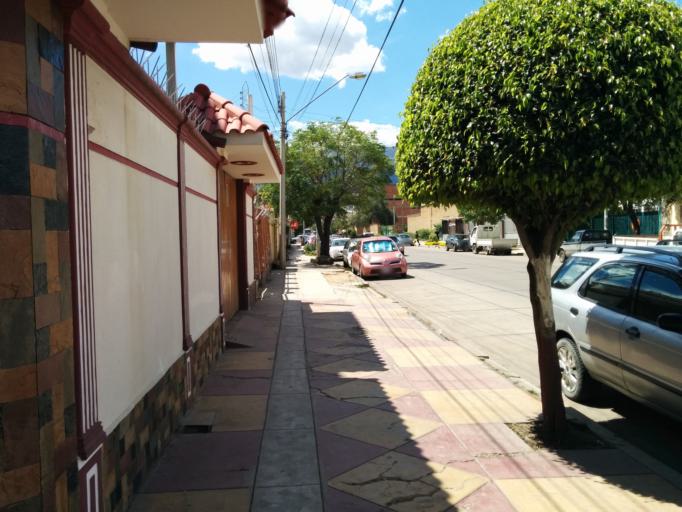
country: BO
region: Cochabamba
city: Cochabamba
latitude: -17.4014
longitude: -66.1666
